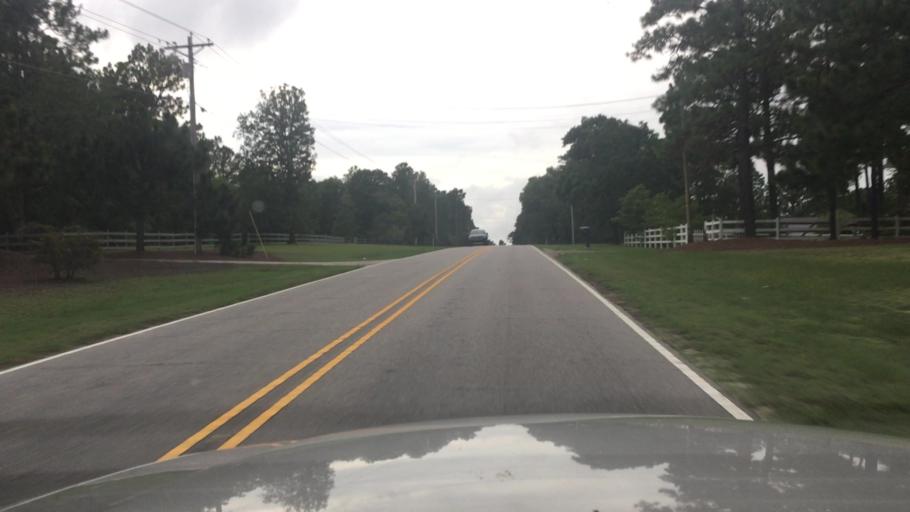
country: US
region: North Carolina
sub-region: Hoke County
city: Rockfish
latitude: 34.9582
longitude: -79.0393
